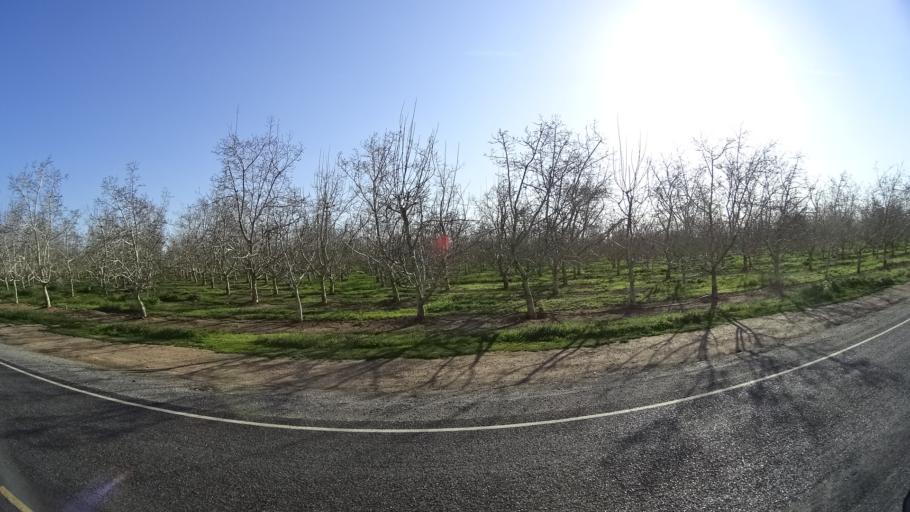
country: US
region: California
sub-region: Glenn County
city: Orland
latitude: 39.7915
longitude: -122.1218
